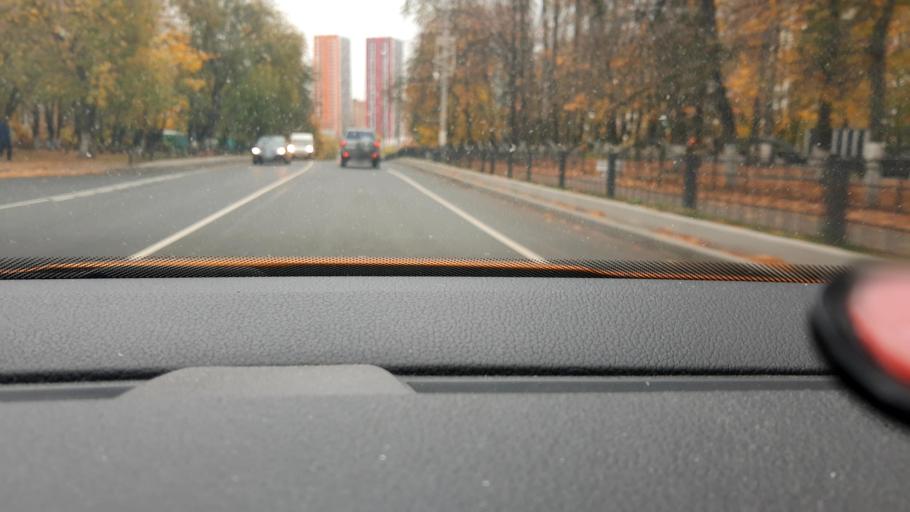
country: RU
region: Moskovskaya
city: Krasnogorsk
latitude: 55.8219
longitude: 37.3385
